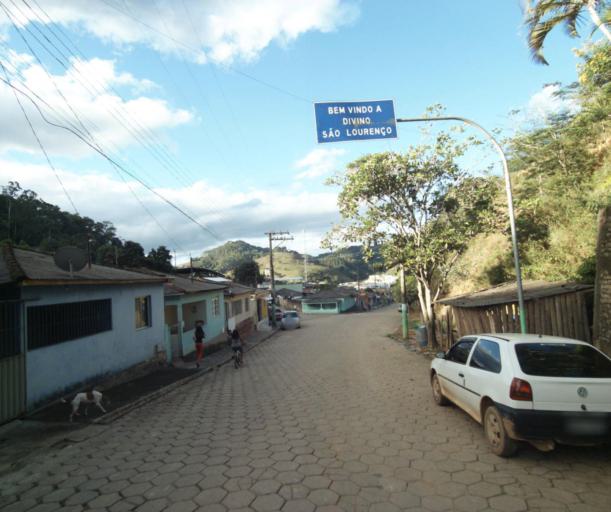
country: BR
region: Espirito Santo
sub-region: Guacui
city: Guacui
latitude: -20.6233
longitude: -41.6869
